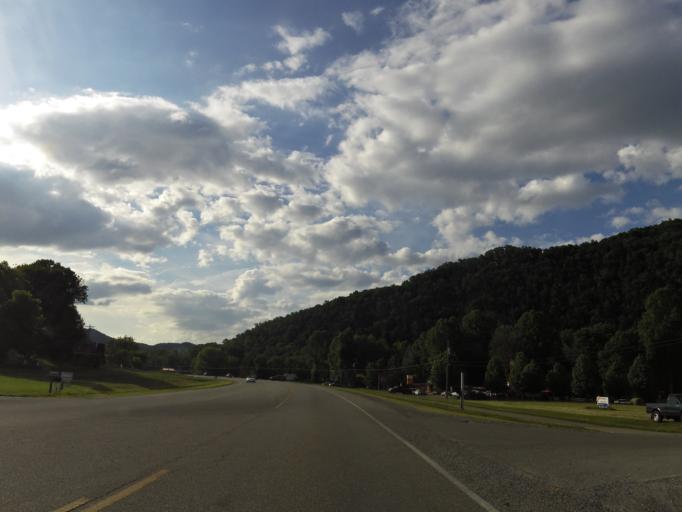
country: US
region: Tennessee
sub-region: Blount County
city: Wildwood
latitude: 35.6758
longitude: -83.7192
